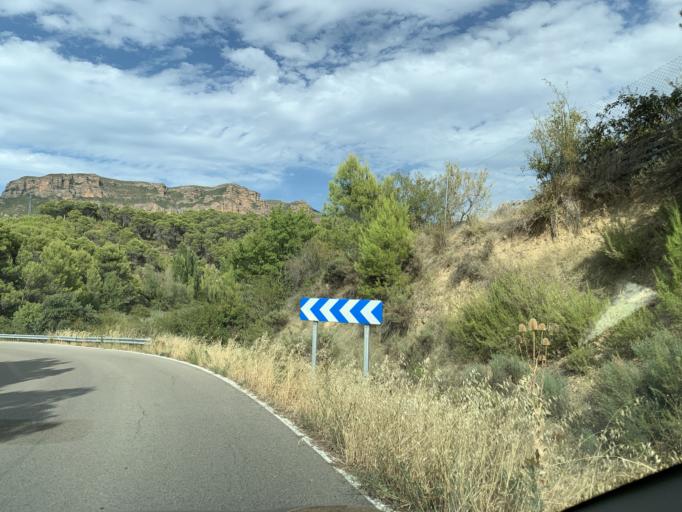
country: ES
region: Aragon
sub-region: Provincia de Zaragoza
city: Santa Eulalia de Gallego
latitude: 42.3196
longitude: -0.7246
